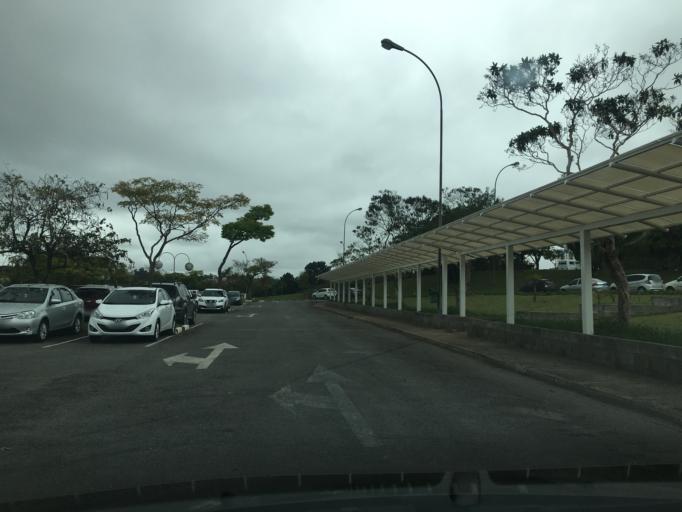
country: BR
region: Sao Paulo
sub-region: Taboao Da Serra
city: Taboao da Serra
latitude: -23.6157
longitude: -46.7718
